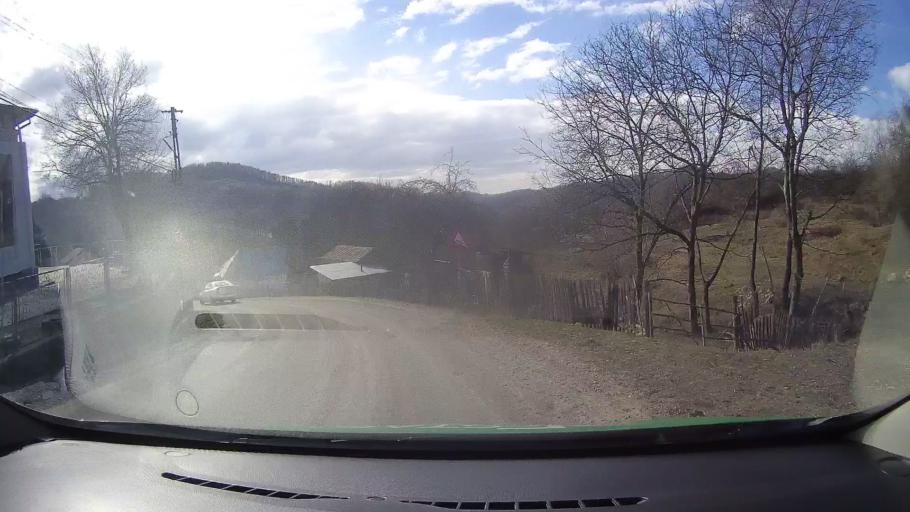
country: RO
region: Dambovita
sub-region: Comuna Varfuri
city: Varfuri
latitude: 45.0939
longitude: 25.5074
